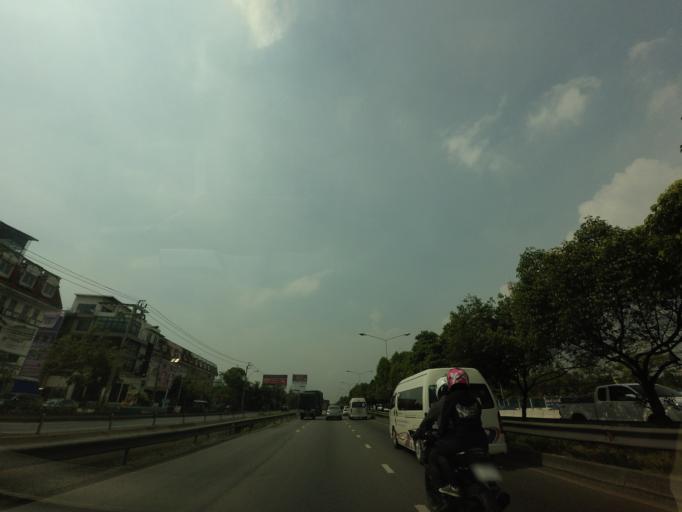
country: TH
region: Bangkok
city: Thawi Watthana
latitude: 13.7877
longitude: 100.3630
